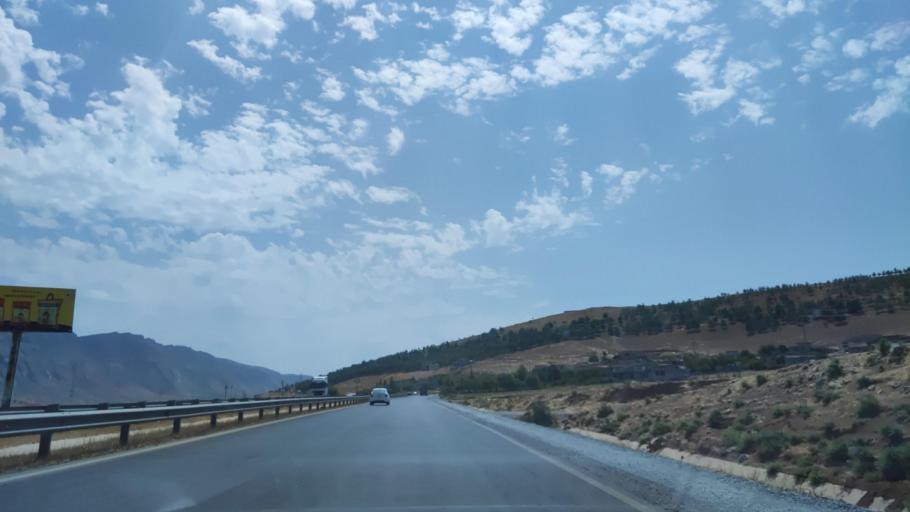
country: IQ
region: Arbil
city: Shaqlawah
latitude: 36.4950
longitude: 44.3666
